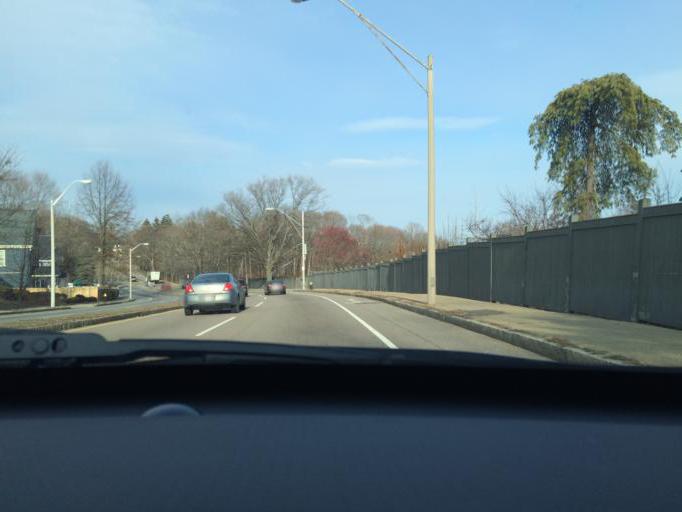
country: US
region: Massachusetts
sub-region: Suffolk County
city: Jamaica Plain
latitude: 42.3029
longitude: -71.1254
